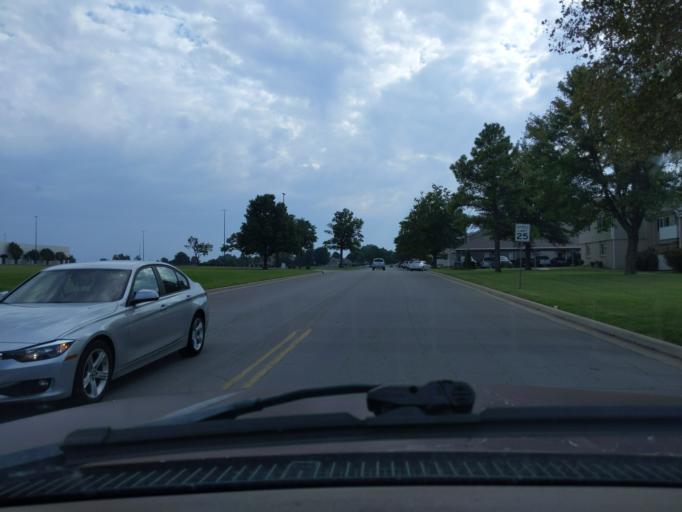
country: US
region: Oklahoma
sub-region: Tulsa County
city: Broken Arrow
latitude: 36.1332
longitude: -95.8234
